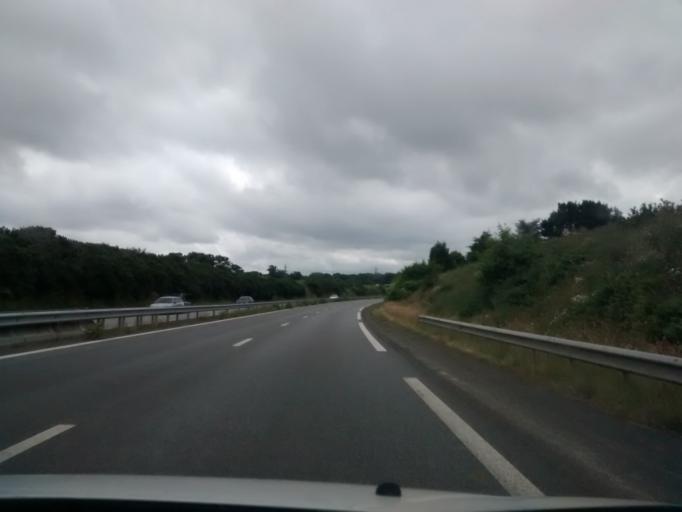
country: FR
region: Brittany
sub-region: Departement d'Ille-et-Vilaine
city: Cesson-Sevigne
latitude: 48.1482
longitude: -1.6244
